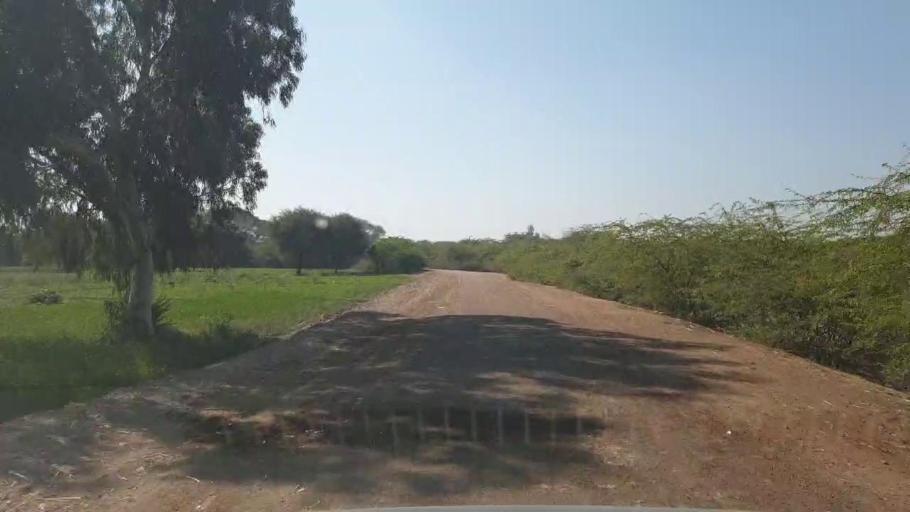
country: PK
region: Sindh
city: Digri
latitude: 25.2658
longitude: 69.2053
